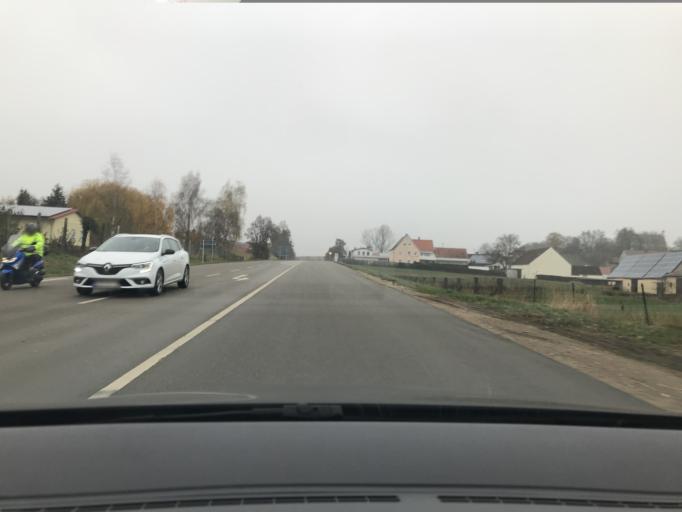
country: DE
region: Bavaria
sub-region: Swabia
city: Marktoffingen
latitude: 48.9240
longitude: 10.4654
